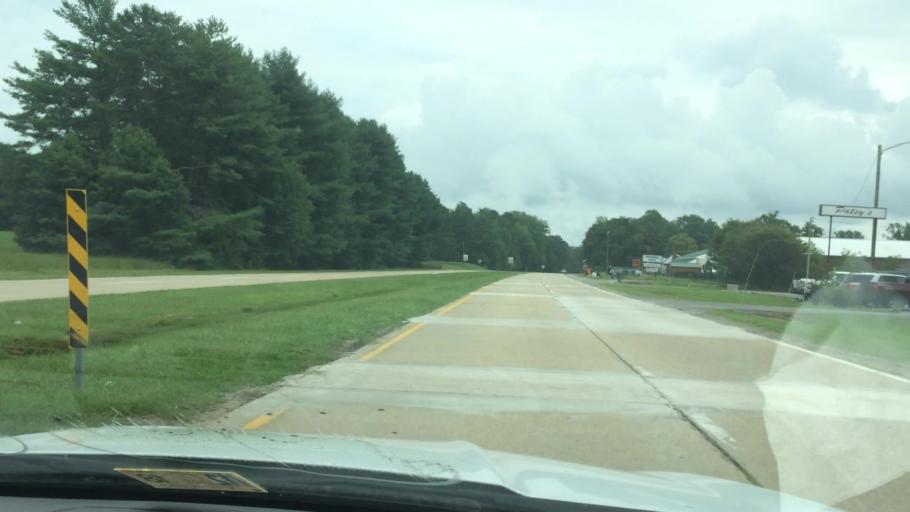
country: US
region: Virginia
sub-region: New Kent County
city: New Kent
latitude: 37.4418
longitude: -77.0373
